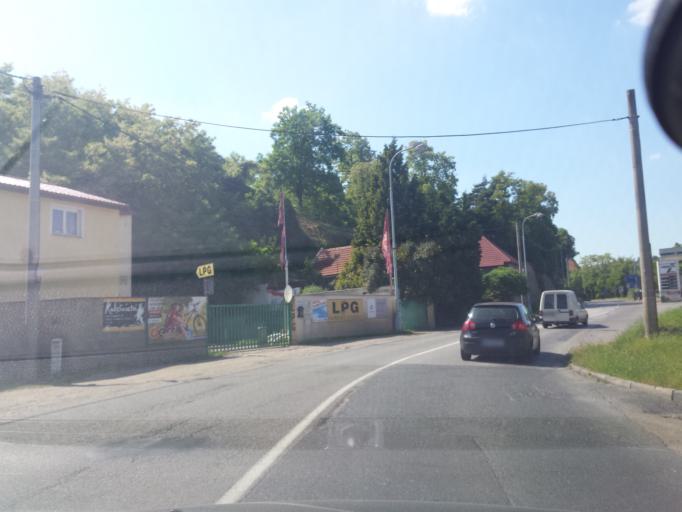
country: CZ
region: Central Bohemia
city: Kralupy nad Vltavou
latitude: 50.2290
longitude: 14.2947
